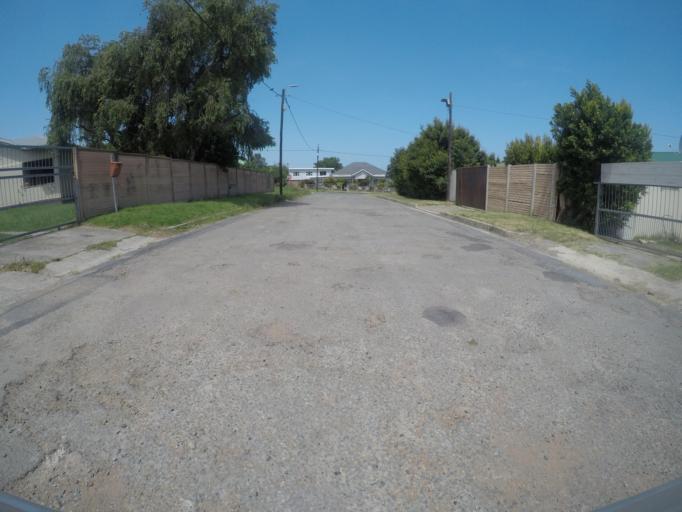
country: ZA
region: Eastern Cape
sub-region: Buffalo City Metropolitan Municipality
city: East London
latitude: -32.9735
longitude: 27.8705
